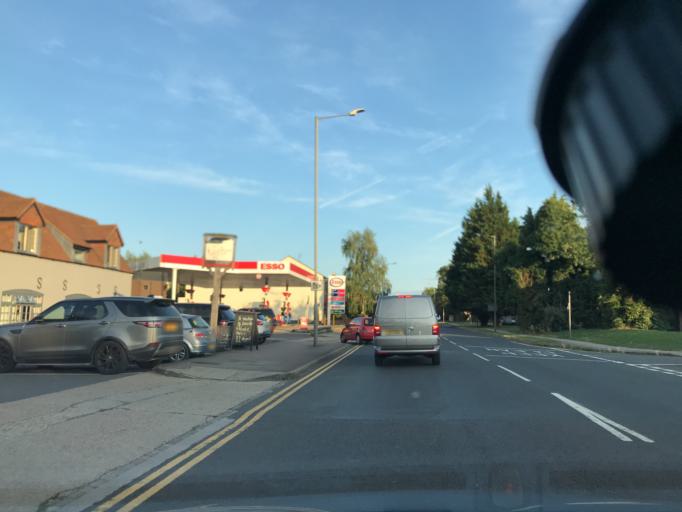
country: GB
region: England
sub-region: Buckinghamshire
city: Aylesbury
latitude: 51.8102
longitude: -0.8044
